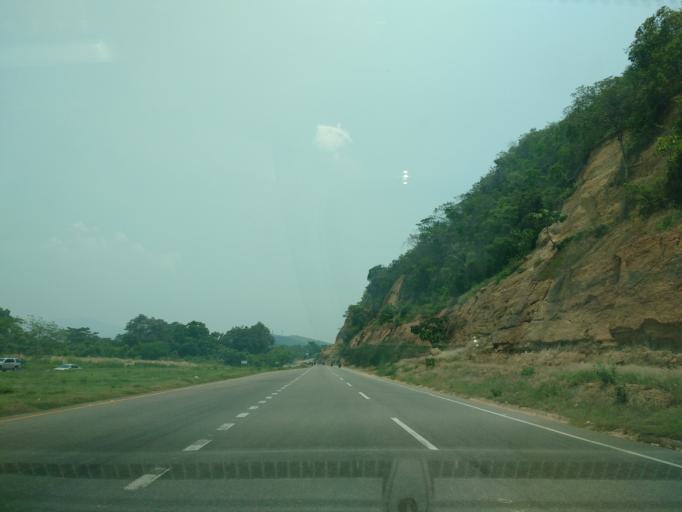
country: CO
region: Tolima
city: Melgar
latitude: 4.2094
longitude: -74.6456
